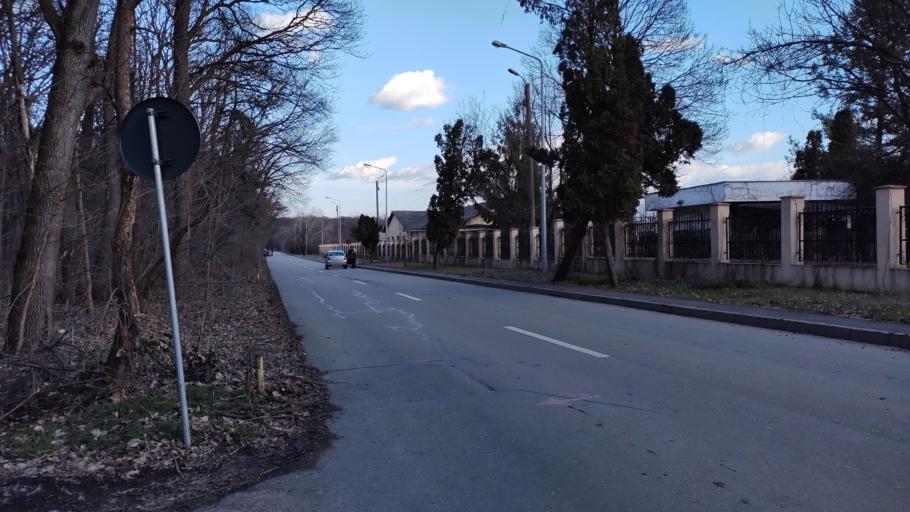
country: RO
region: Ilfov
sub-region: Comuna Otopeni
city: Otopeni
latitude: 44.5231
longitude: 26.0816
